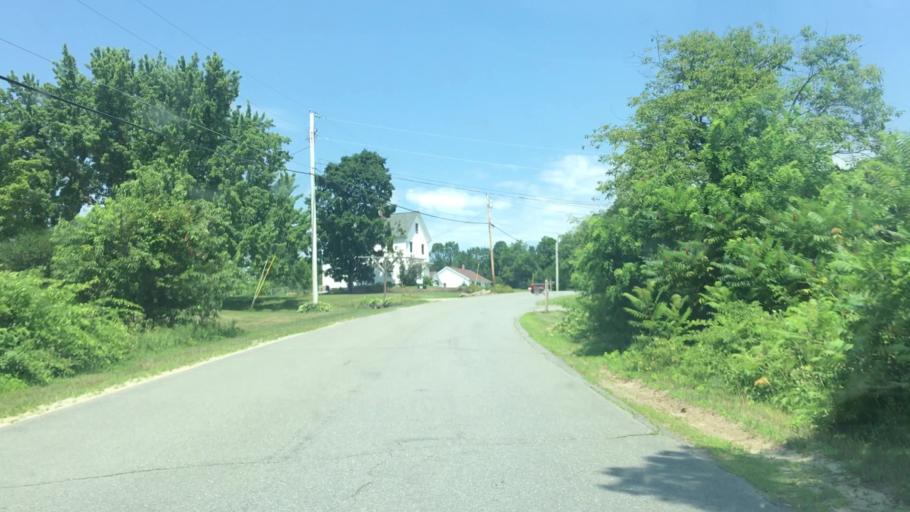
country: US
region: Maine
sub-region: Kennebec County
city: Monmouth
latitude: 44.2756
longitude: -70.0498
